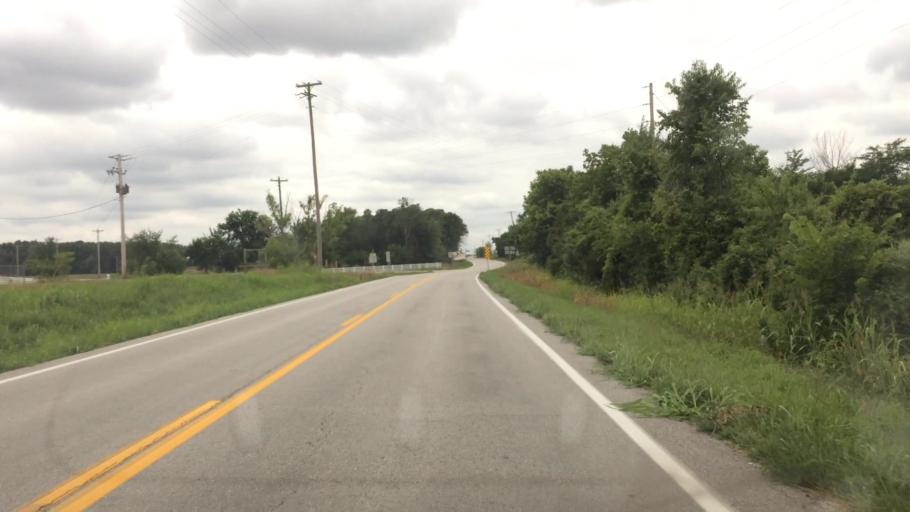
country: US
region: Missouri
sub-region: Greene County
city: Strafford
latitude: 37.2822
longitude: -93.1132
